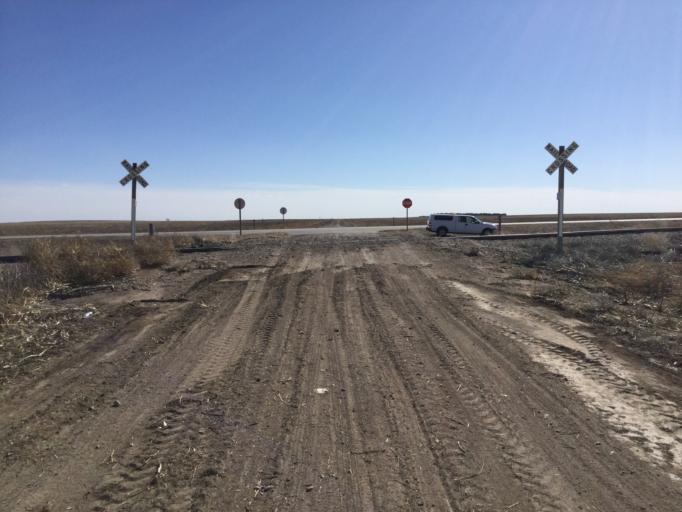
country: US
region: Kansas
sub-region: Sheridan County
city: Hoxie
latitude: 39.5272
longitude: -100.6084
